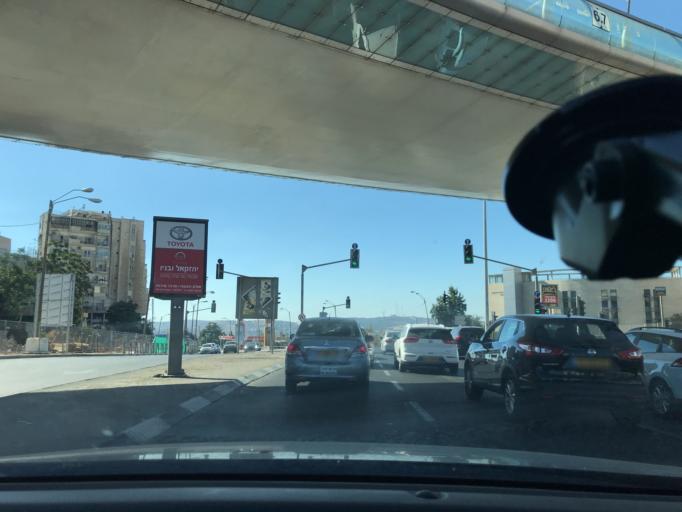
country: IL
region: Jerusalem
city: West Jerusalem
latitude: 31.7885
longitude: 35.2000
